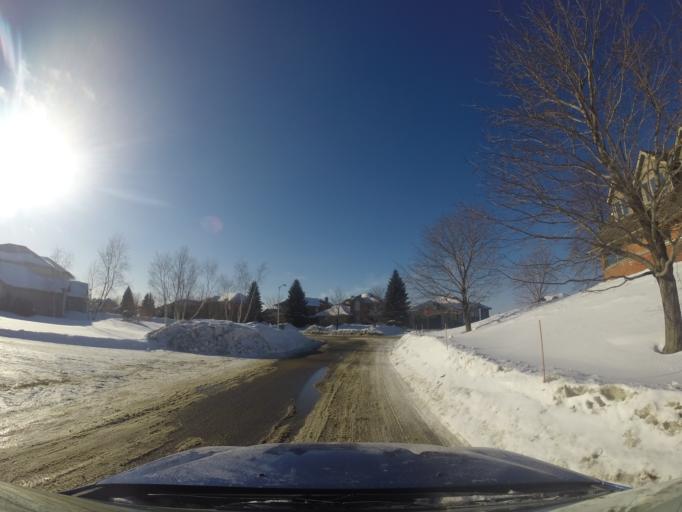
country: CA
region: Ontario
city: Greater Sudbury
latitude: 46.4577
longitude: -80.9905
